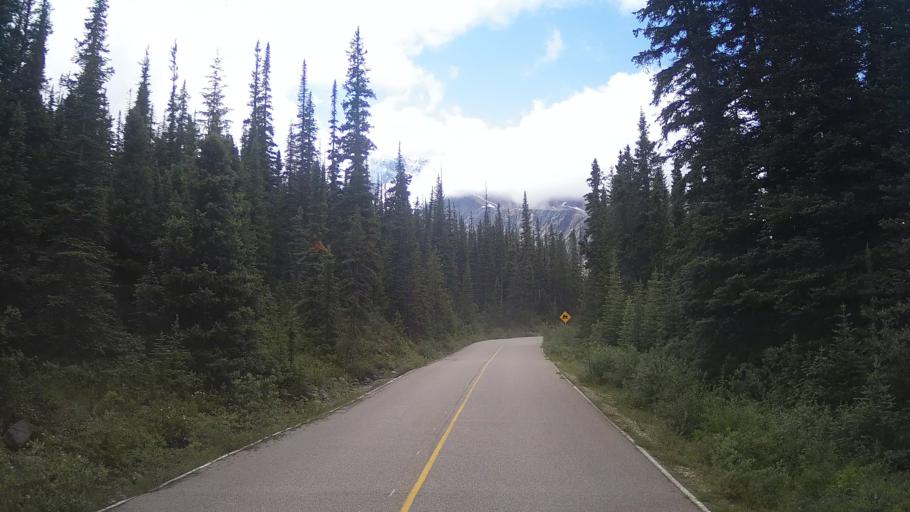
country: CA
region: Alberta
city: Jasper Park Lodge
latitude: 52.7196
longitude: -118.0525
